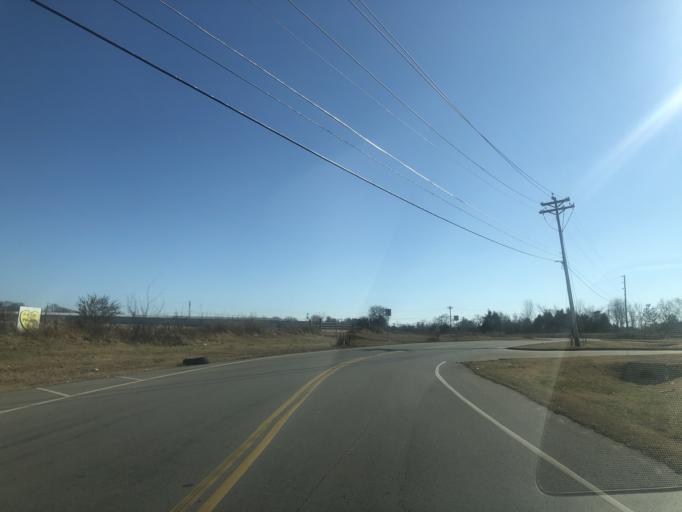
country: US
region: Tennessee
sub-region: Rutherford County
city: Smyrna
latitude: 35.9361
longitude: -86.5294
